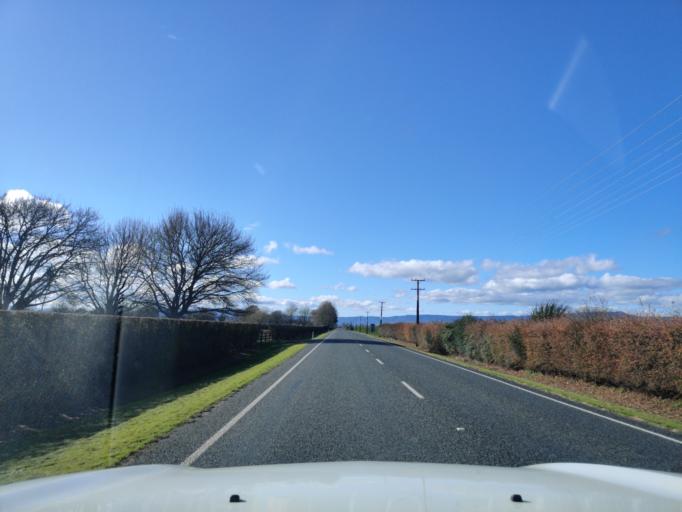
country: NZ
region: Waikato
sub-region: Matamata-Piako District
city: Matamata
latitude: -37.8781
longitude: 175.7380
